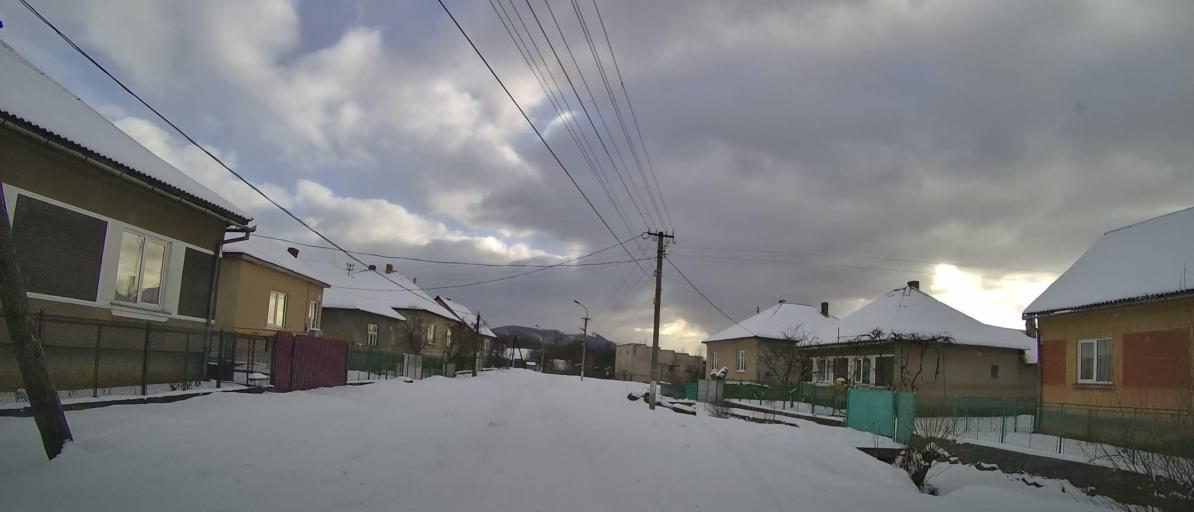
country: UA
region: Zakarpattia
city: Velykyi Bereznyi
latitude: 48.9141
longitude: 22.4641
